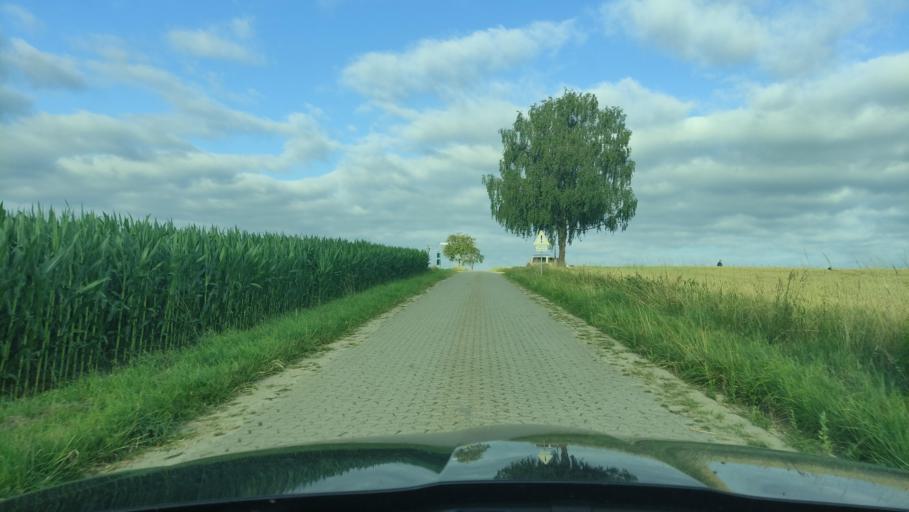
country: DE
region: Bavaria
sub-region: Swabia
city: Roggenburg
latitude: 48.2746
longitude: 10.2555
